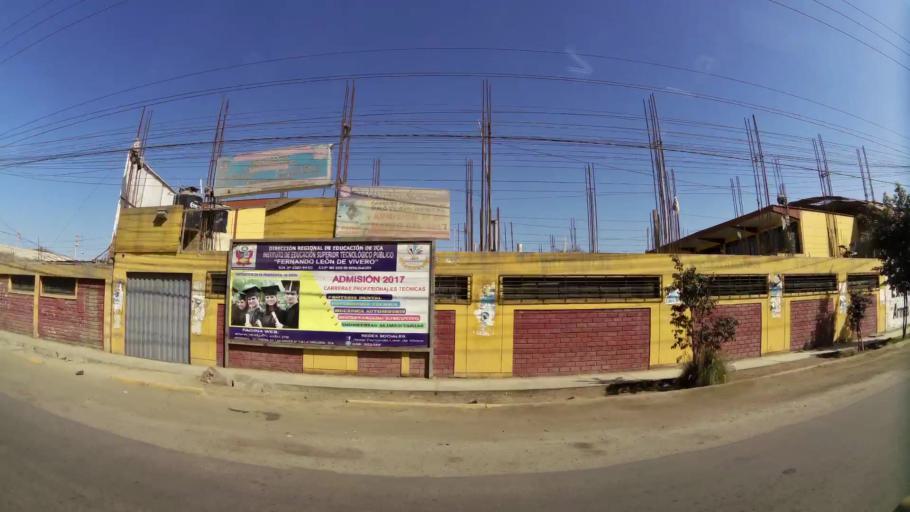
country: PE
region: Ica
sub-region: Provincia de Ica
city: La Tinguina
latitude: -14.0394
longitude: -75.7111
